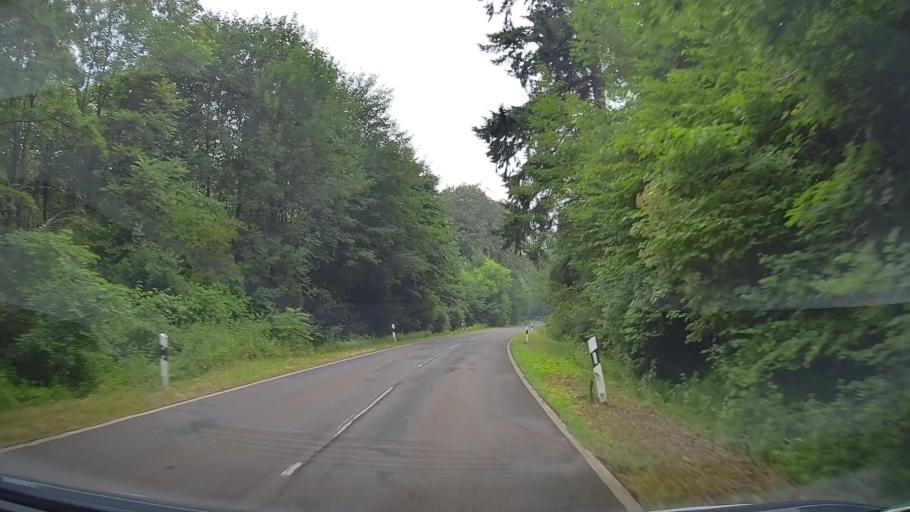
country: DE
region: Lower Saxony
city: Rinteln
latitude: 52.1535
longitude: 9.0318
